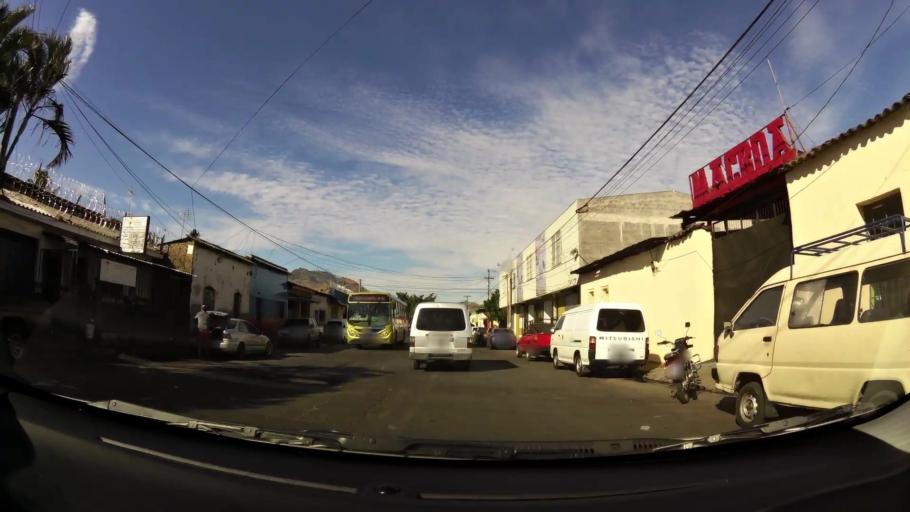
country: SV
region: Santa Ana
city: Santa Ana
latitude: 13.9862
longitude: -89.5658
